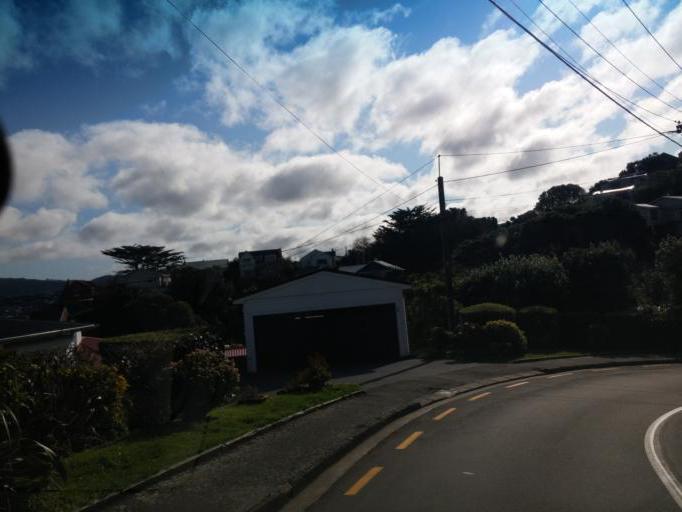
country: NZ
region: Wellington
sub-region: Wellington City
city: Wellington
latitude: -41.3235
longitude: 174.8247
